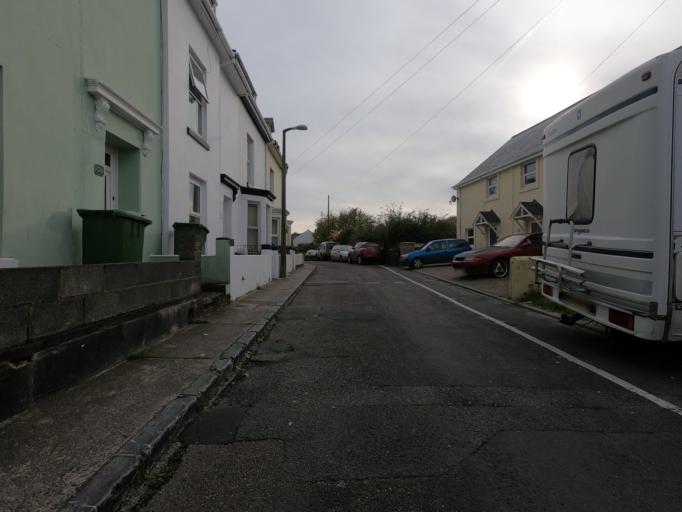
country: GB
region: England
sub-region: Borough of Torbay
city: Brixham
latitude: 50.3931
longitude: -3.5145
